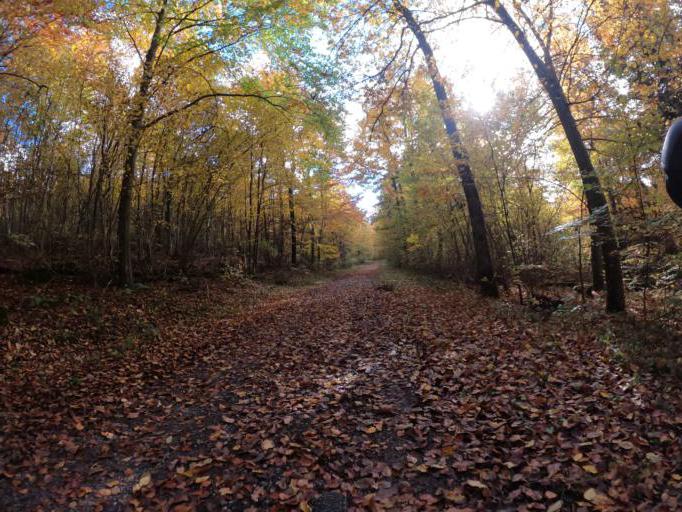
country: DE
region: Baden-Wuerttemberg
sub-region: Regierungsbezirk Stuttgart
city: Aidlingen
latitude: 48.7053
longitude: 8.9026
